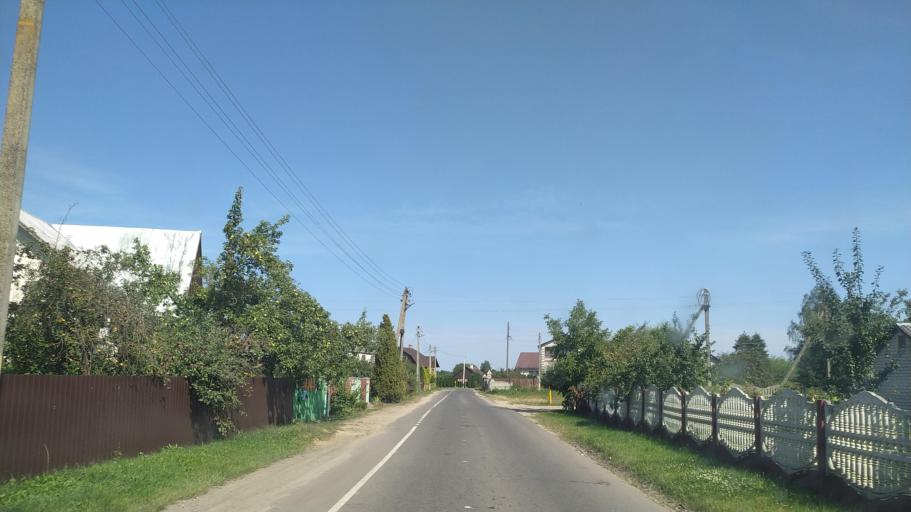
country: BY
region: Brest
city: Byaroza
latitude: 52.5292
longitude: 24.9936
